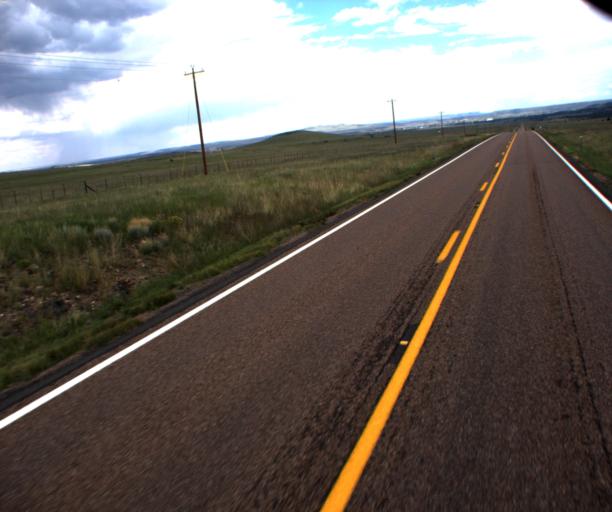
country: US
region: Arizona
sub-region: Apache County
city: Eagar
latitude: 34.0983
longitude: -109.3999
